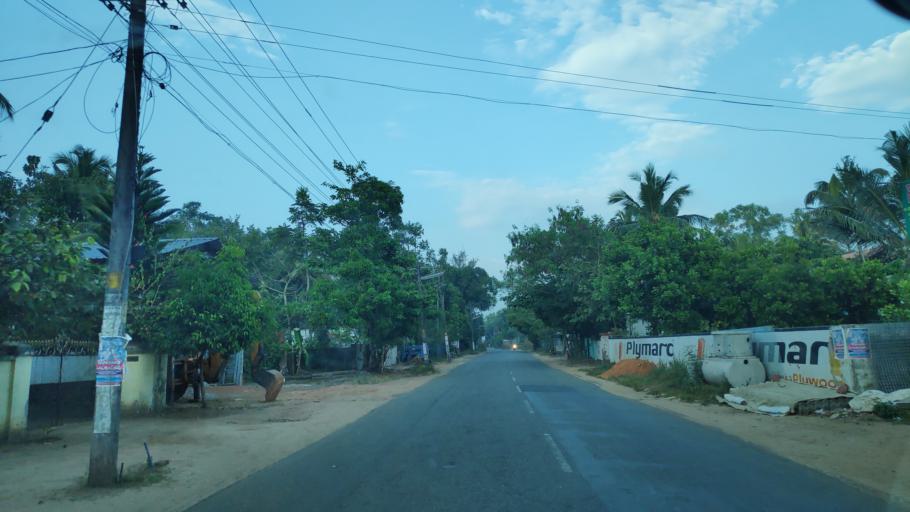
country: IN
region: Kerala
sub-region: Alappuzha
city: Shertallai
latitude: 9.6313
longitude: 76.3703
